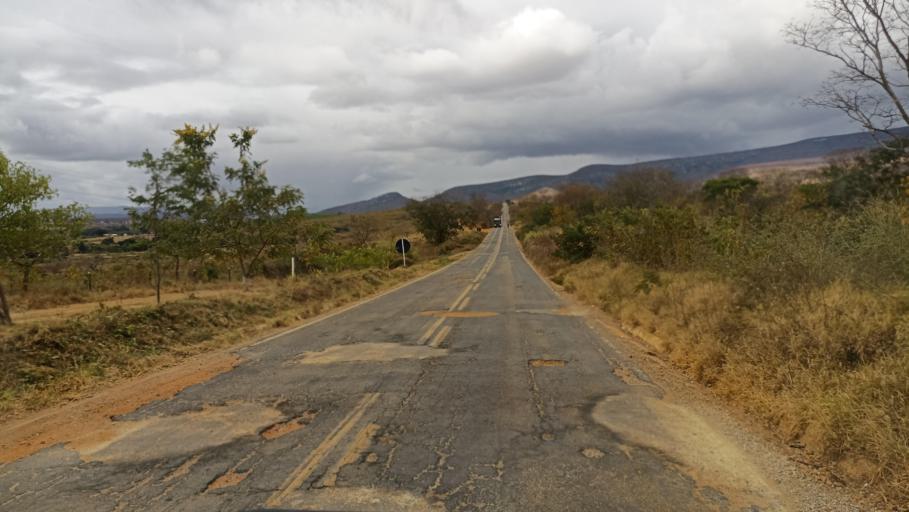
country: BR
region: Minas Gerais
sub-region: Itinga
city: Itinga
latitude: -16.6298
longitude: -41.7921
